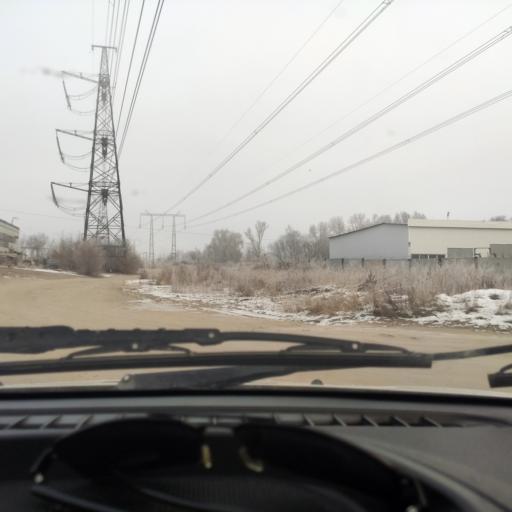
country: RU
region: Samara
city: Zhigulevsk
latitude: 53.4769
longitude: 49.5048
